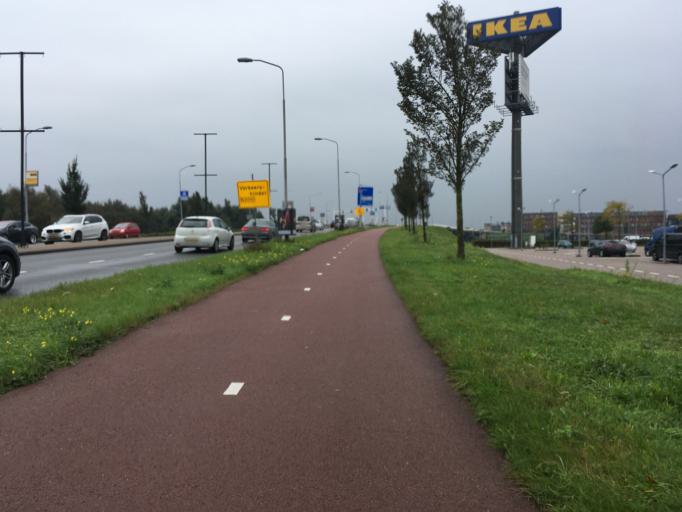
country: NL
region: North Holland
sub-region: Gemeente Haarlem
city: Haarlem
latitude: 52.3854
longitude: 4.6723
